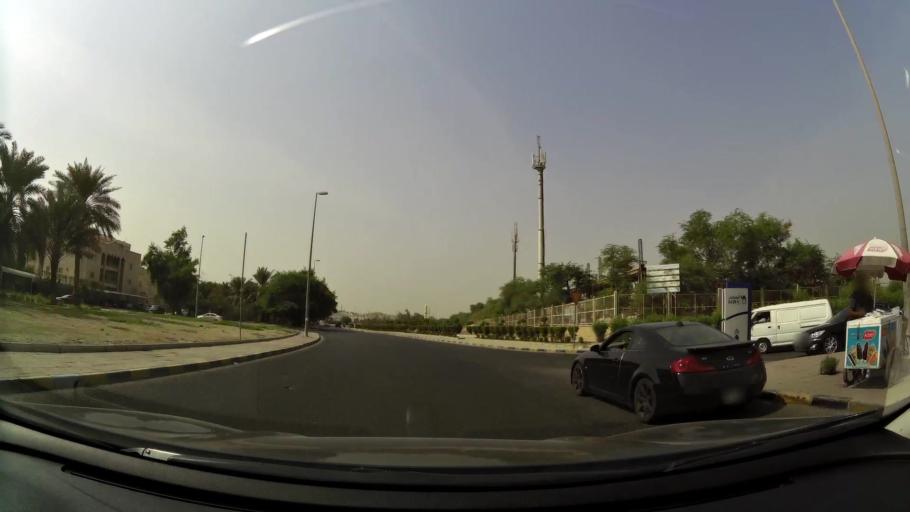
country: KW
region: Al Asimah
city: Ar Rabiyah
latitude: 29.3034
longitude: 47.8886
